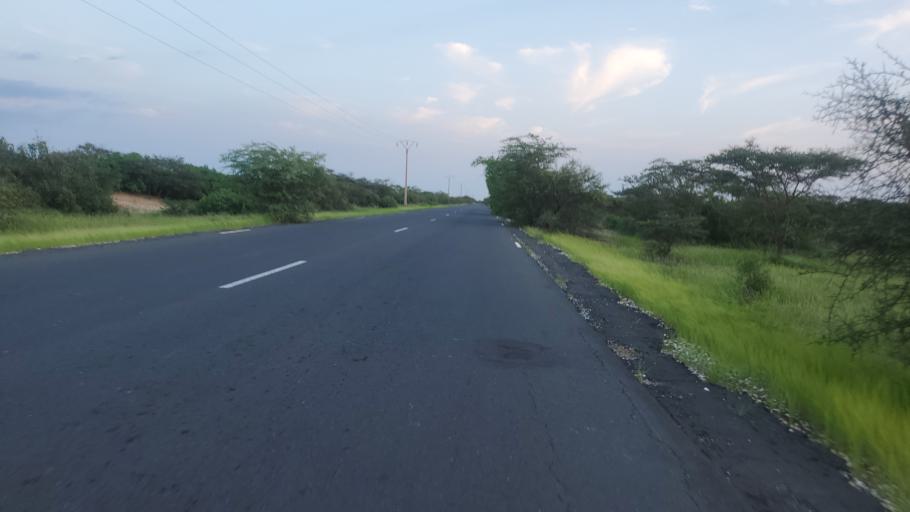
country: SN
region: Saint-Louis
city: Saint-Louis
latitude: 16.1159
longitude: -16.4136
